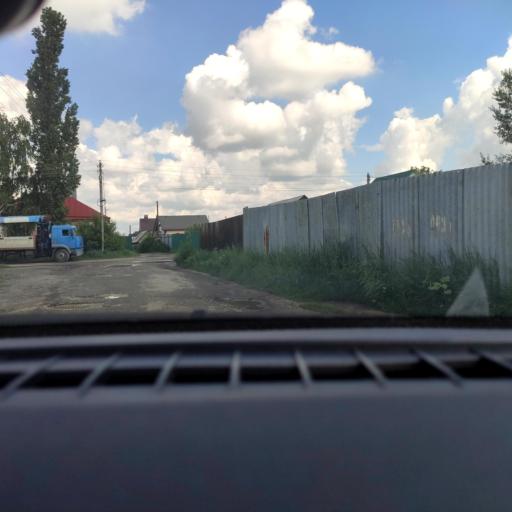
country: RU
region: Voronezj
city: Novaya Usman'
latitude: 51.6813
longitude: 39.3749
